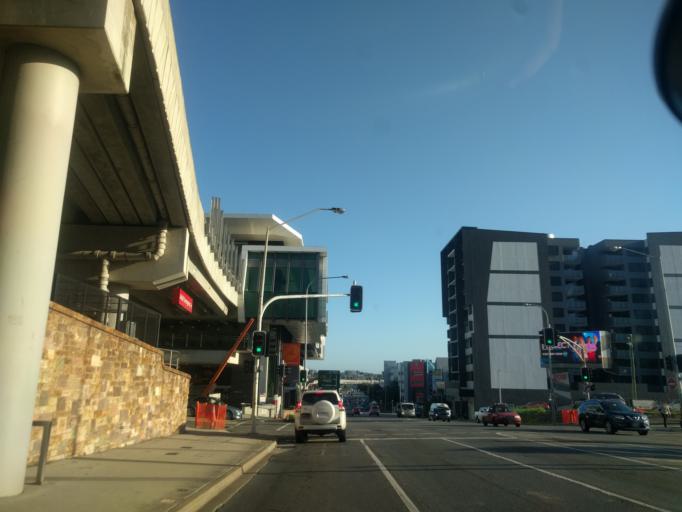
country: AU
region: Queensland
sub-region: Brisbane
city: Fortitude Valley
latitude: -27.4482
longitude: 153.0292
